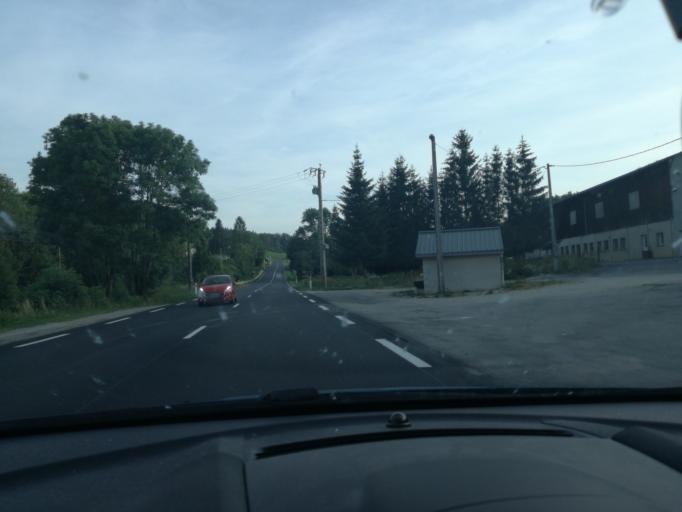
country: FR
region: Franche-Comte
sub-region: Departement du Jura
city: Morbier
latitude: 46.6004
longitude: 5.9608
